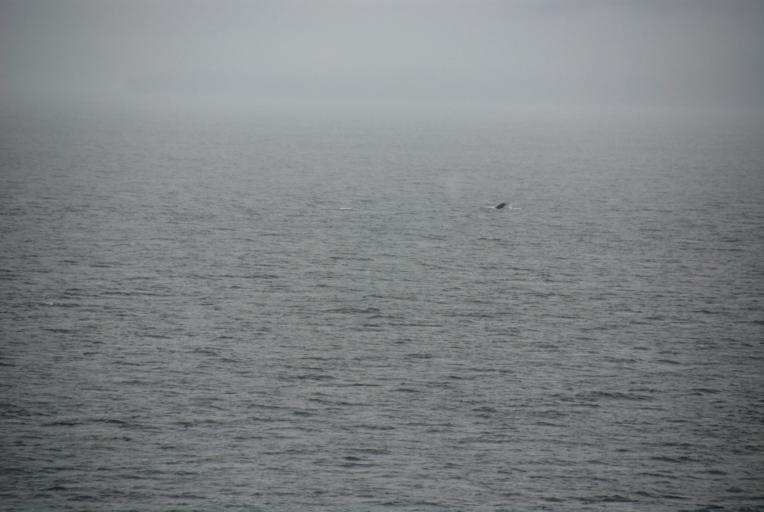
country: US
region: Alaska
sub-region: Sitka City and Borough
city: Sitka
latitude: 57.1150
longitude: -134.1254
